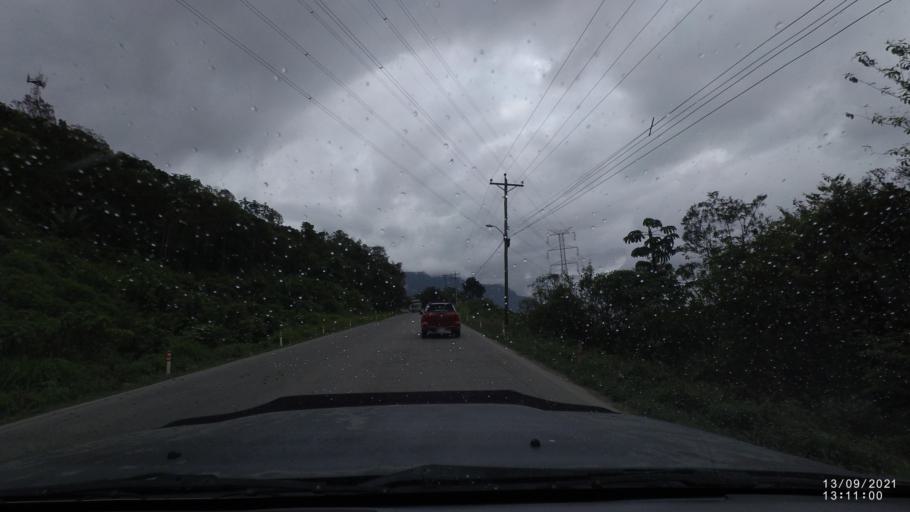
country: BO
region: Cochabamba
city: Colomi
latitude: -17.2045
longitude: -65.8292
